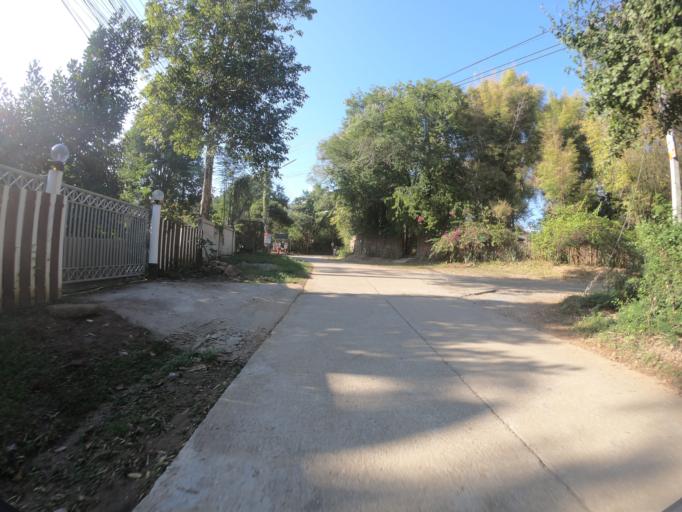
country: TH
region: Chiang Mai
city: Chiang Mai
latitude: 18.7712
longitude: 98.9425
